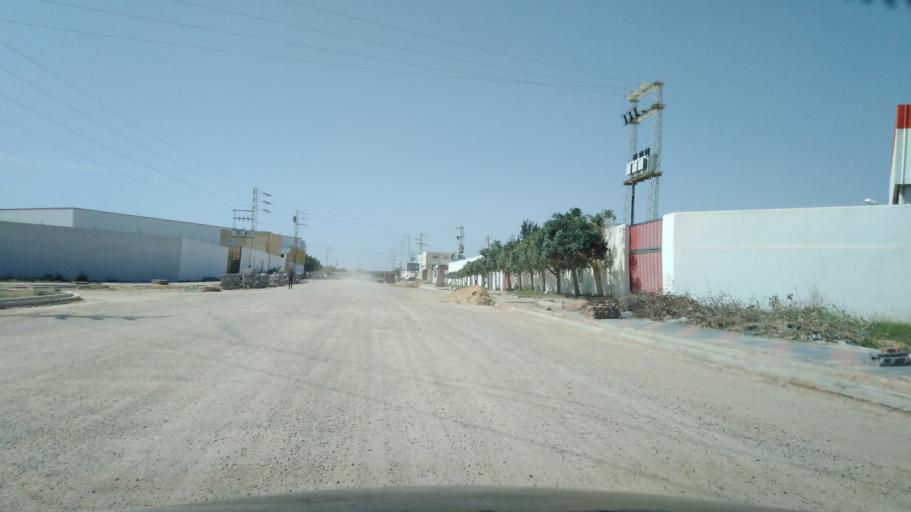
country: TN
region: Safaqis
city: Sfax
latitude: 34.7288
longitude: 10.5150
